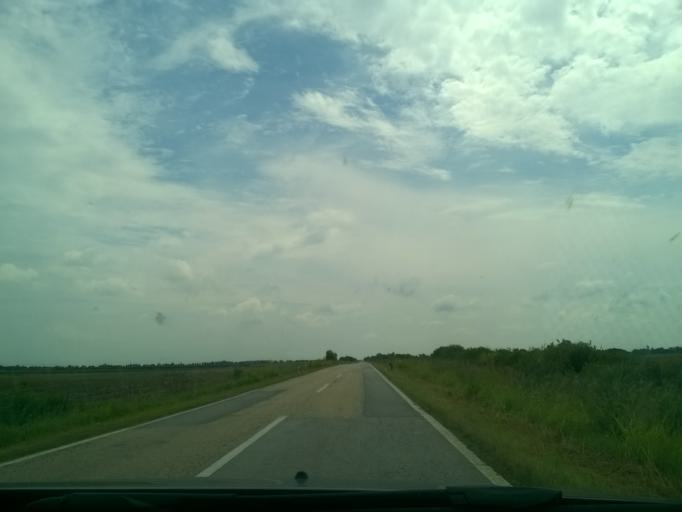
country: RS
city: Stari Lec
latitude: 45.2838
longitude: 20.9377
